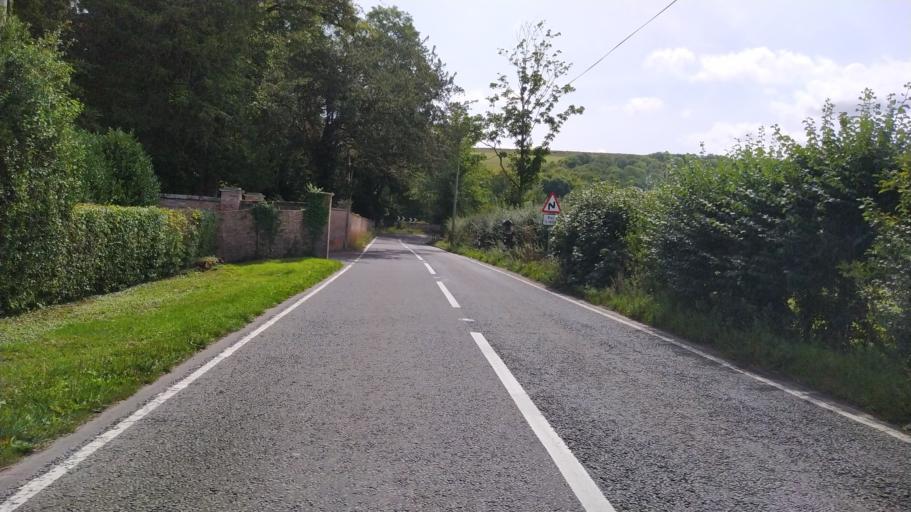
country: GB
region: England
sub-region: Dorset
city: Blandford Forum
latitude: 50.9024
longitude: -2.1984
